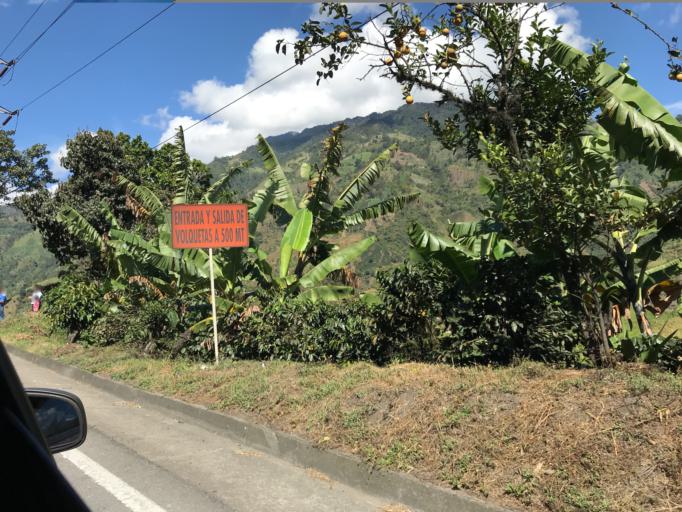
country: CO
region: Tolima
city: Cajamarca
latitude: 4.4433
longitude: -75.4106
